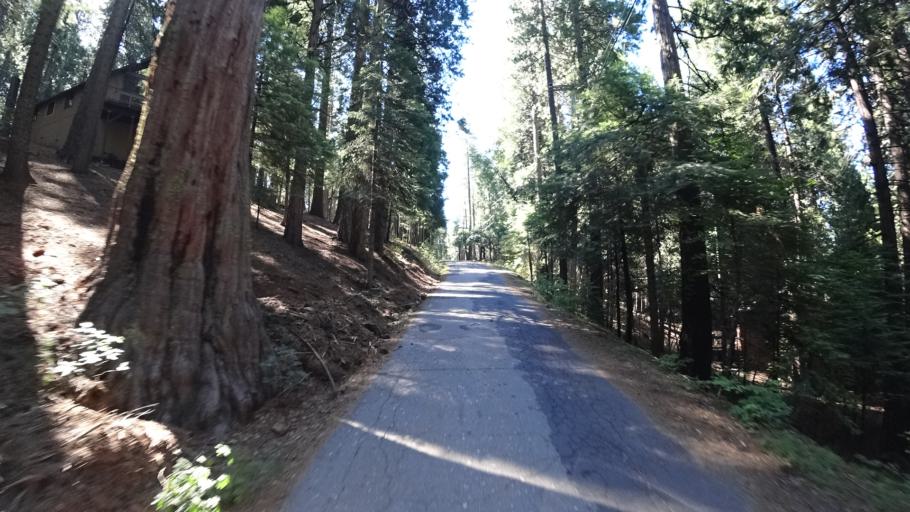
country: US
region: California
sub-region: Calaveras County
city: Arnold
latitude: 38.2960
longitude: -120.2724
